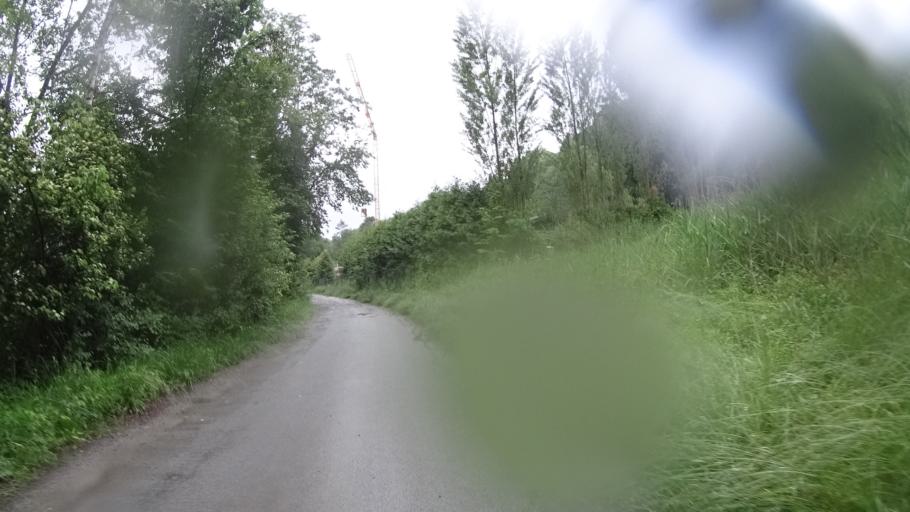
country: DE
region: Bavaria
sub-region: Lower Bavaria
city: Passau
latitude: 48.5112
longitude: 13.4541
